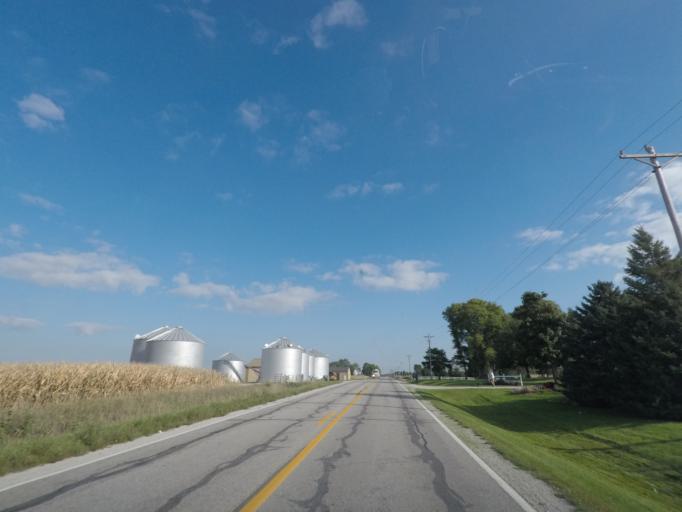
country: US
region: Iowa
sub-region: Story County
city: Nevada
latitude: 41.9968
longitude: -93.4628
